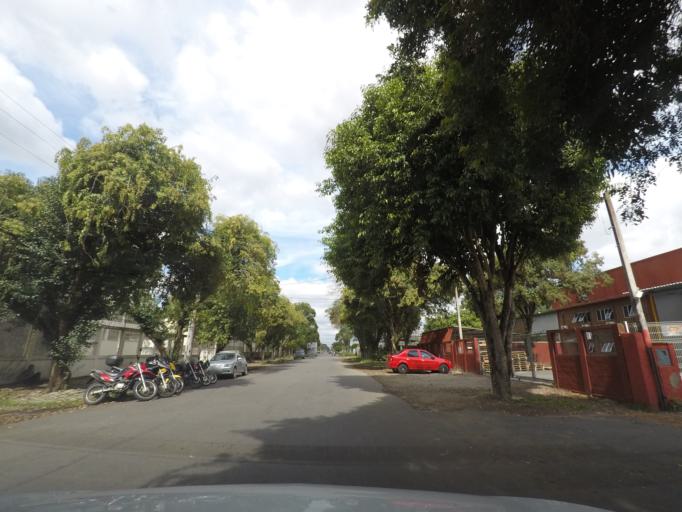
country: BR
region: Parana
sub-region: Sao Jose Dos Pinhais
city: Sao Jose dos Pinhais
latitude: -25.4899
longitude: -49.2406
